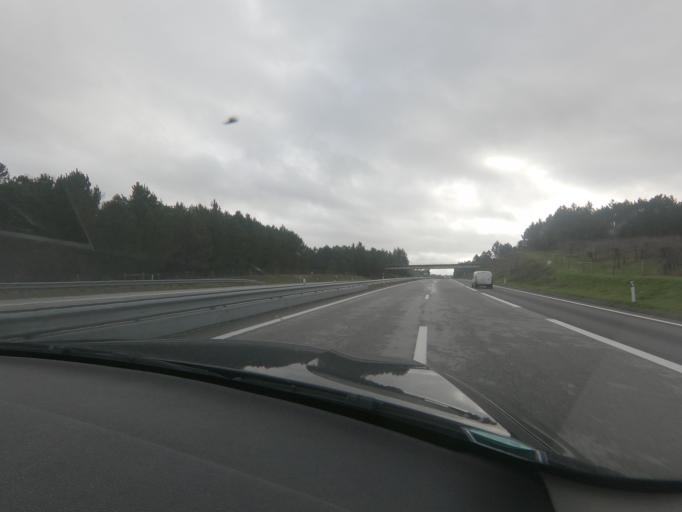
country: PT
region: Viseu
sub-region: Viseu
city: Campo
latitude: 40.7307
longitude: -7.9216
